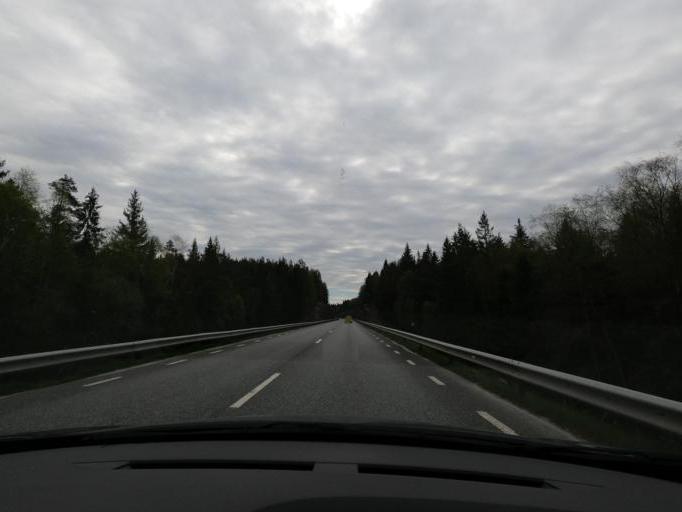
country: SE
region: Vaestra Goetaland
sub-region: Tranemo Kommun
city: Langhem
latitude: 57.5762
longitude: 13.2262
